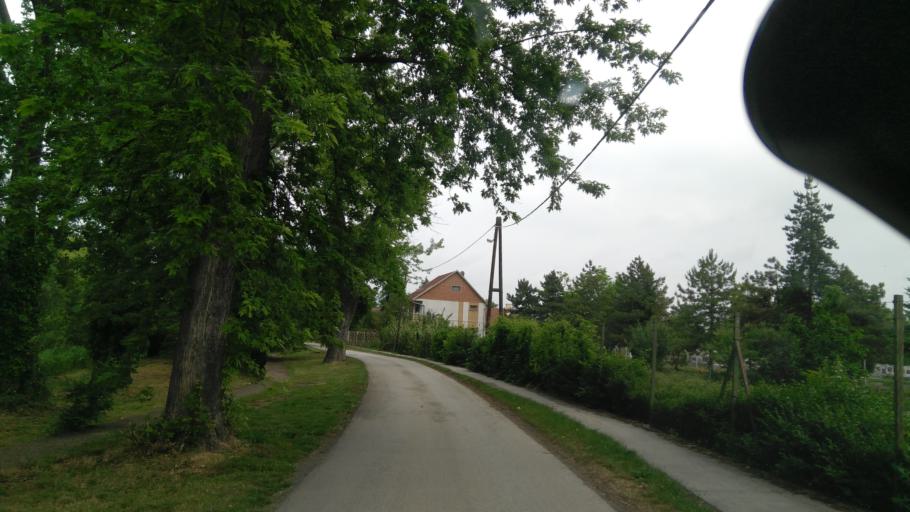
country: HU
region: Bekes
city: Bekescsaba
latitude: 46.6868
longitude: 21.1003
